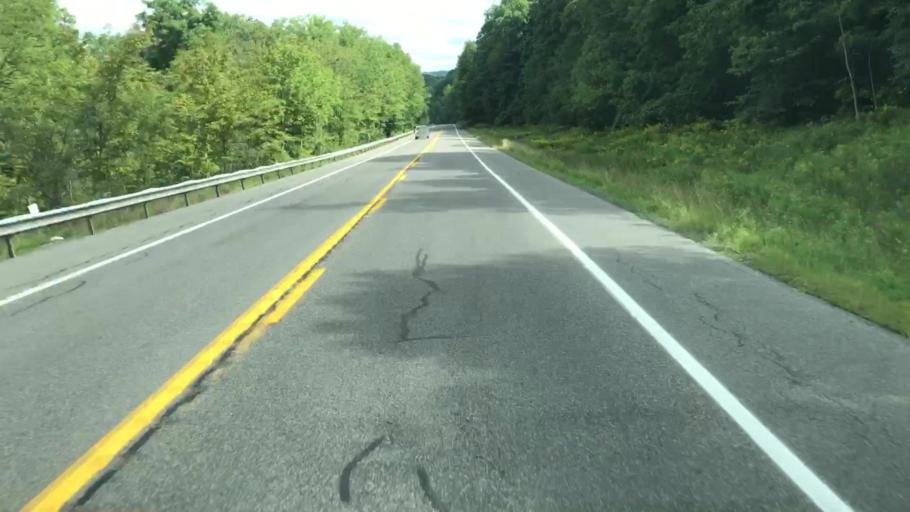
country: US
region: New York
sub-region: Onondaga County
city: Marcellus
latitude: 42.9531
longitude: -76.3639
